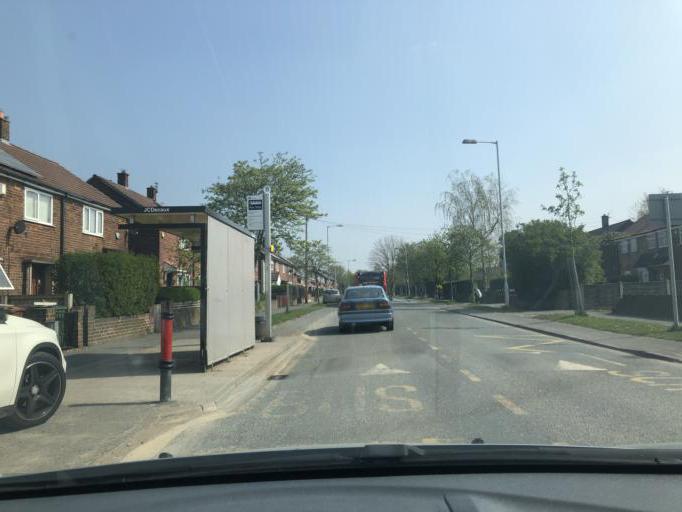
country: GB
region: England
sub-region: Borough of Stockport
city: Bredbury
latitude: 53.4317
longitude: -2.1346
